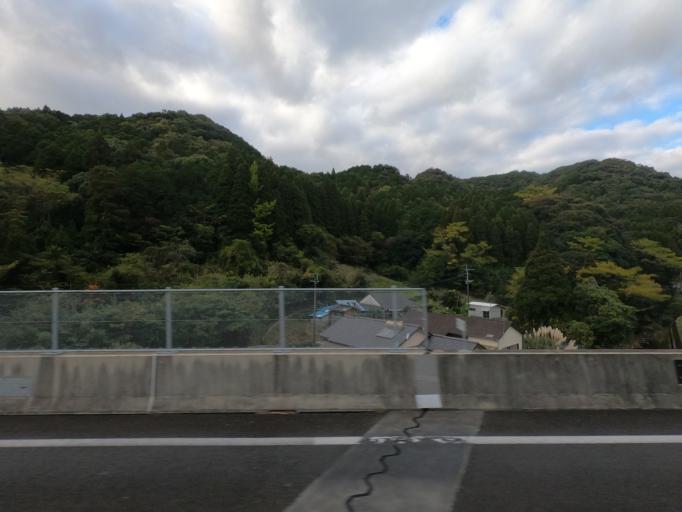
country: JP
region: Kumamoto
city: Minamata
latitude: 32.2360
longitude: 130.4569
